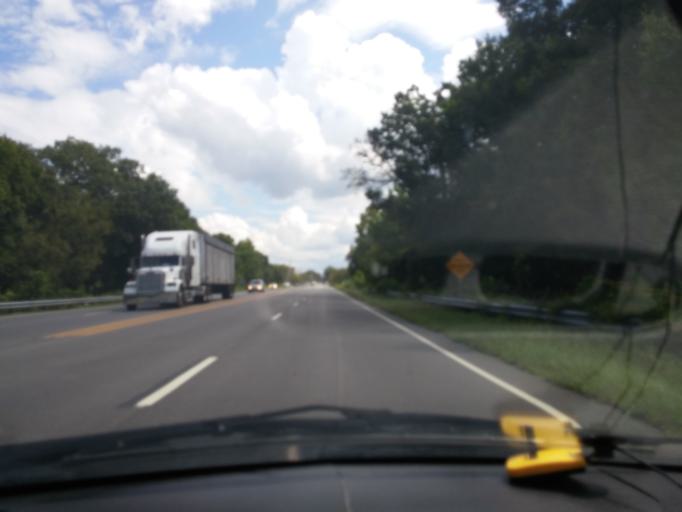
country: US
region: North Carolina
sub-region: Lenoir County
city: Kinston
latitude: 35.2588
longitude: -77.5867
